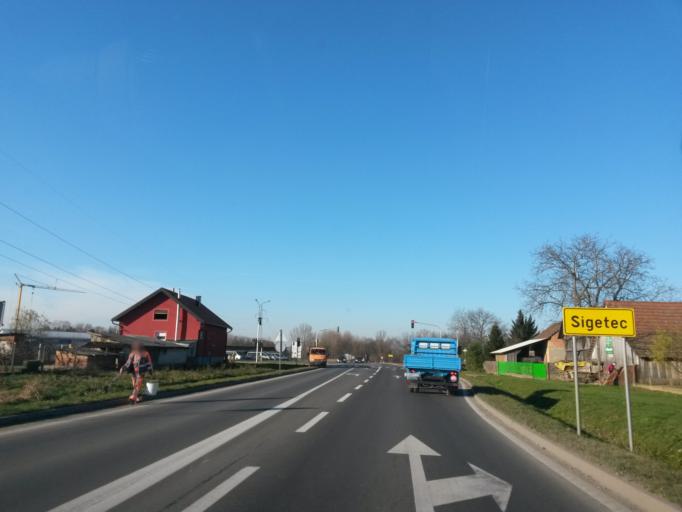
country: HR
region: Varazdinska
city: Ludbreg
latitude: 46.2528
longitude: 16.6353
